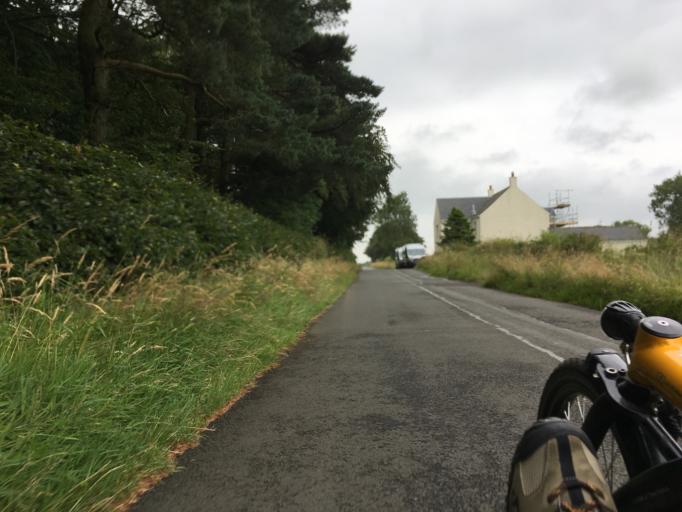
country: GB
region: Scotland
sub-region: West Lothian
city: West Calder
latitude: 55.8442
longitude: -3.5194
